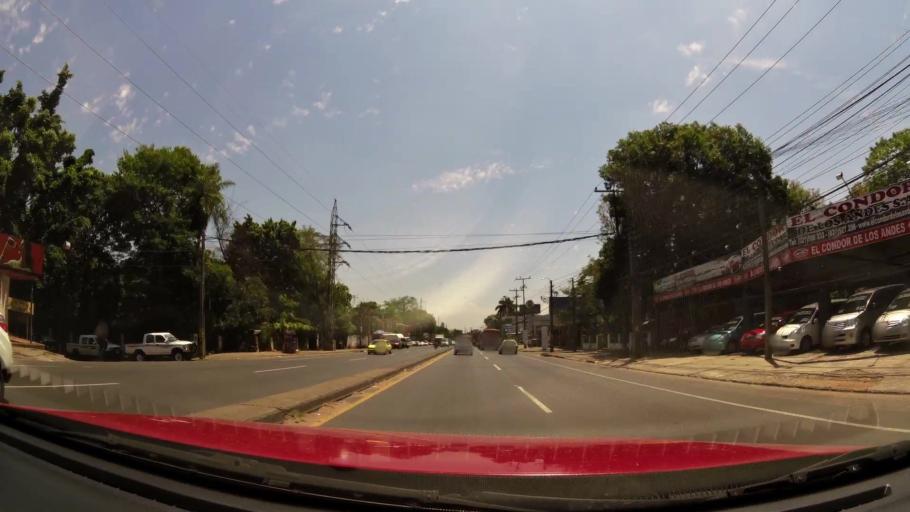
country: PY
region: Central
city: Villa Elisa
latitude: -25.3467
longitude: -57.5774
